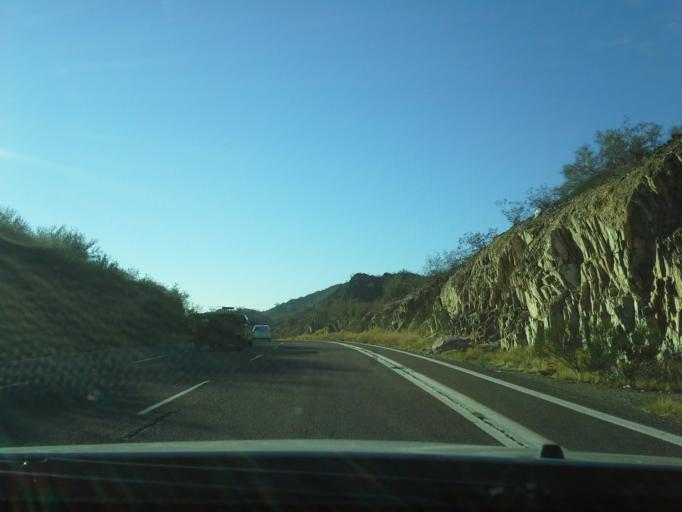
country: US
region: Arizona
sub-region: Maricopa County
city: Glendale
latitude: 33.5922
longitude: -112.0665
